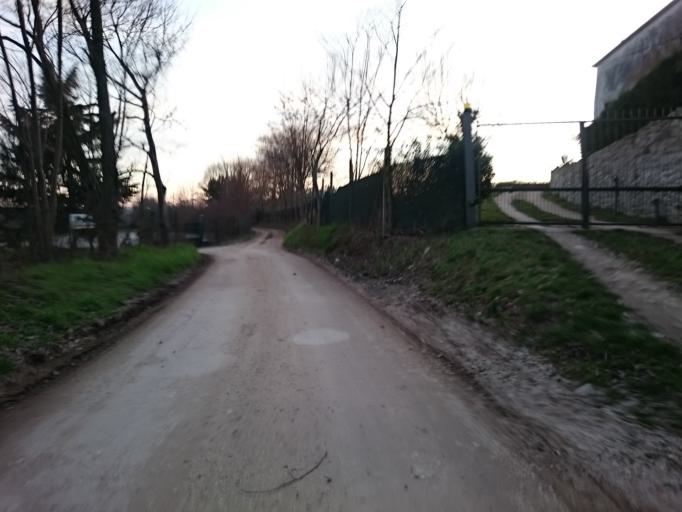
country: IT
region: Veneto
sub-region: Provincia di Verona
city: Castelnuovo del Garda
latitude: 45.4249
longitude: 10.7596
